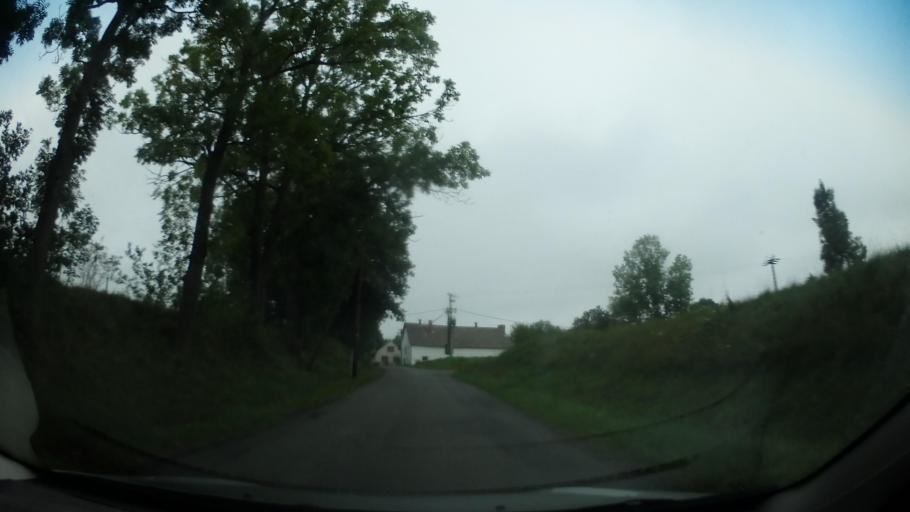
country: CZ
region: Central Bohemia
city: Sedlcany
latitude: 49.7087
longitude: 14.3738
